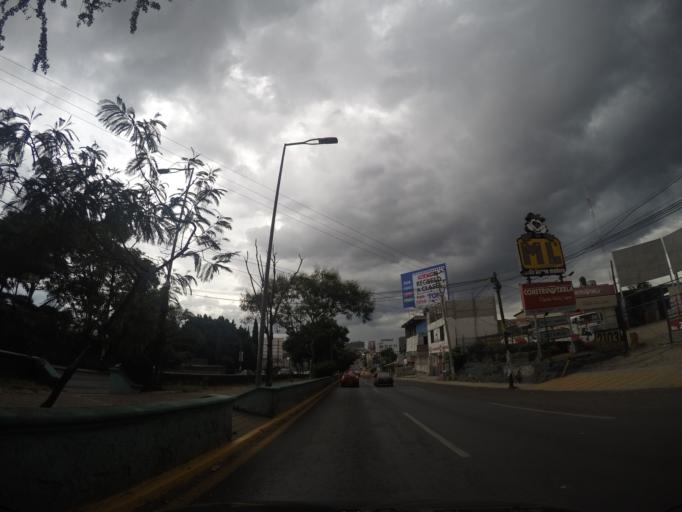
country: MX
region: Oaxaca
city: Oaxaca de Juarez
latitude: 17.0699
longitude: -96.7059
